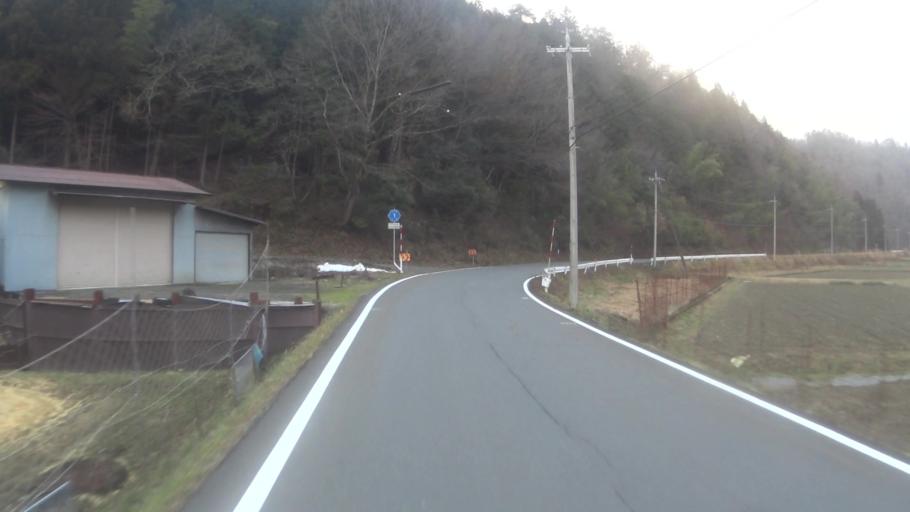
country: JP
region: Kyoto
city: Maizuru
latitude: 35.3896
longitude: 135.4624
